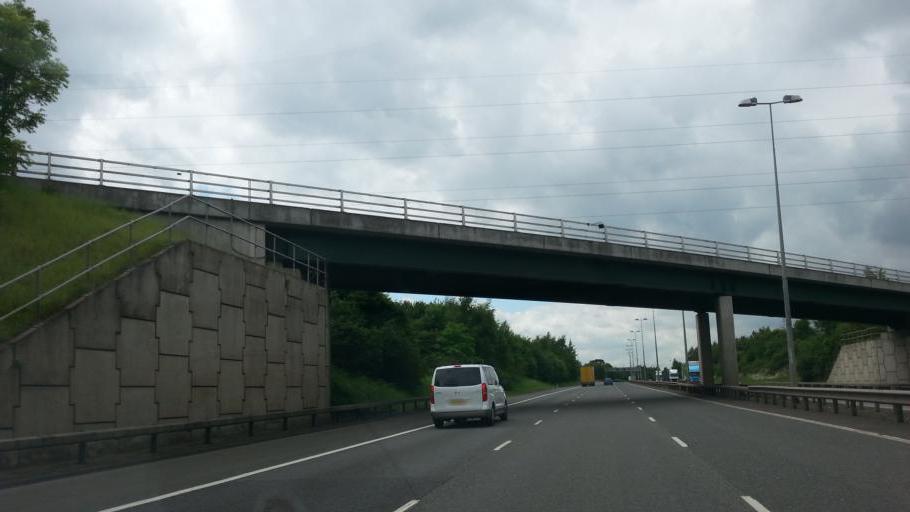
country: GB
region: England
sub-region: Solihull
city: Chelmsley Wood
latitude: 52.4789
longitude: -1.6955
